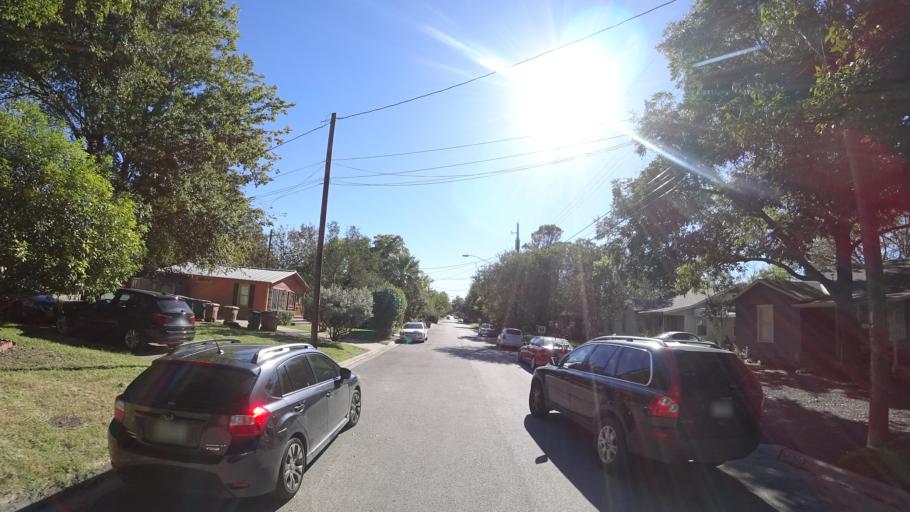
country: US
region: Texas
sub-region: Travis County
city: Austin
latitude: 30.3285
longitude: -97.7347
